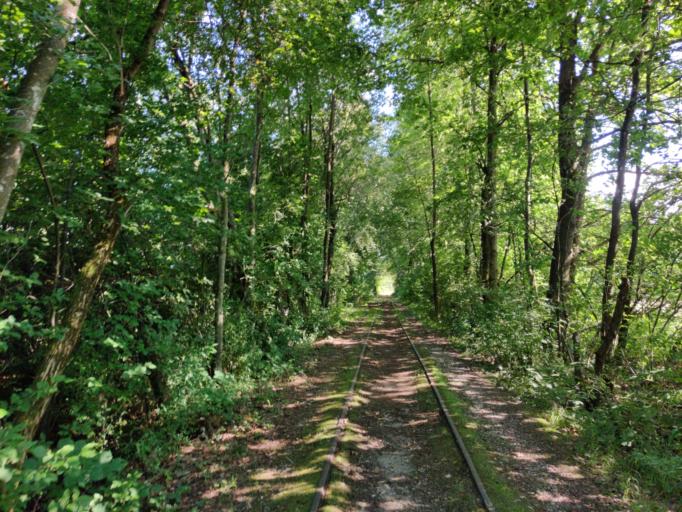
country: AT
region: Carinthia
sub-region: Klagenfurt am Woerthersee
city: Klagenfurt am Woerthersee
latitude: 46.6152
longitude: 14.2584
